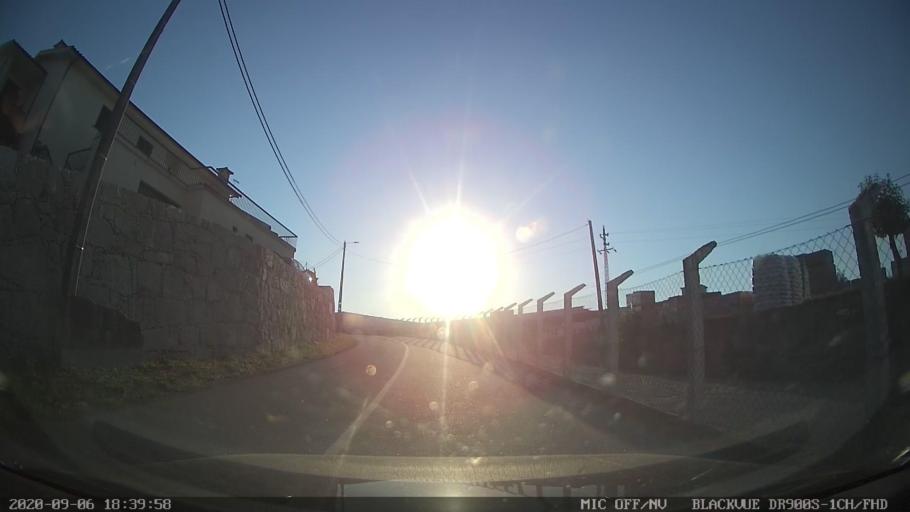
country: PT
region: Porto
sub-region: Amarante
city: Amarante
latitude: 41.2542
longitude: -8.0283
